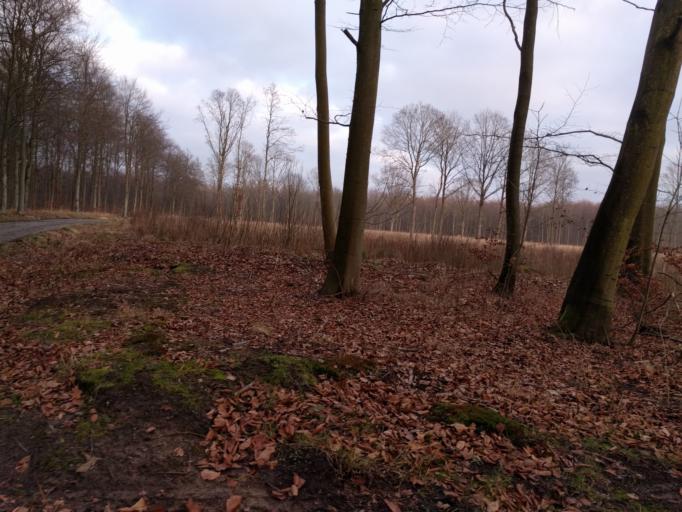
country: DK
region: Zealand
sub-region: Guldborgsund Kommune
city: Stubbekobing
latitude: 54.7768
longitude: 12.0106
